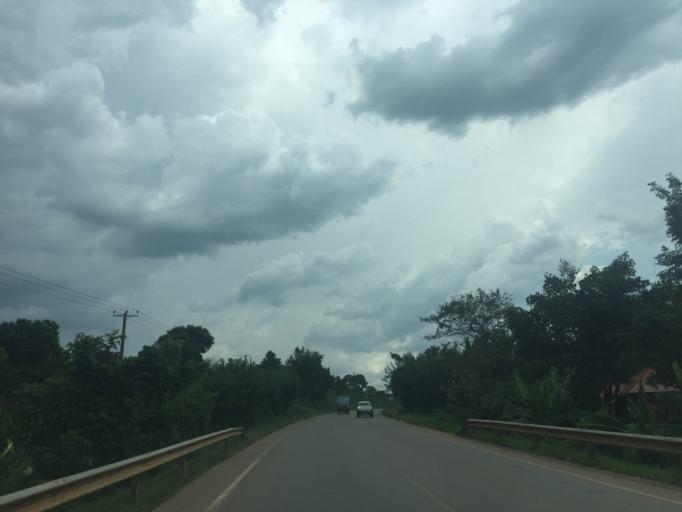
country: UG
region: Central Region
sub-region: Luwero District
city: Wobulenzi
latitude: 0.6742
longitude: 32.5279
